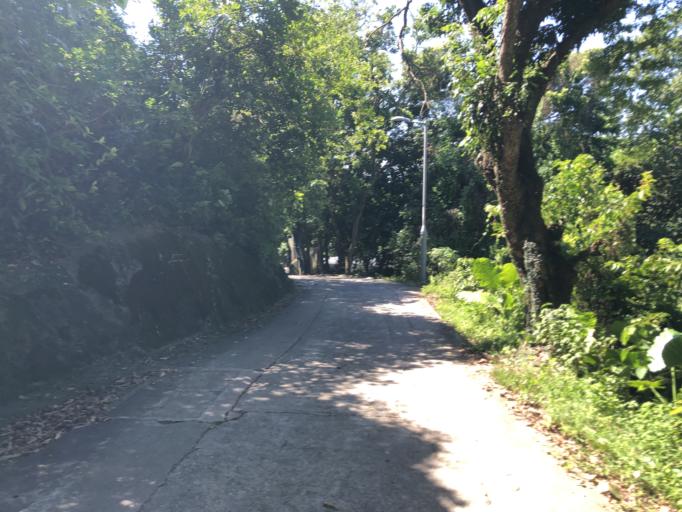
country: HK
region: Tuen Mun
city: Tuen Mun
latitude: 22.2968
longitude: 113.9698
